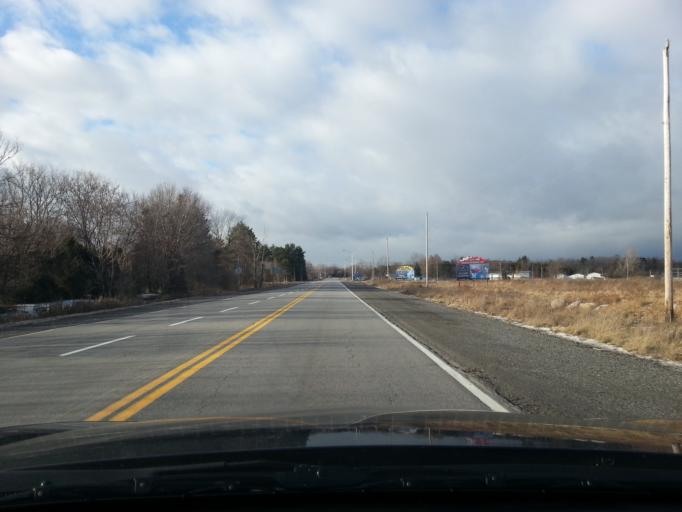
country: CA
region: Ontario
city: Ottawa
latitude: 45.2621
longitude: -75.5531
